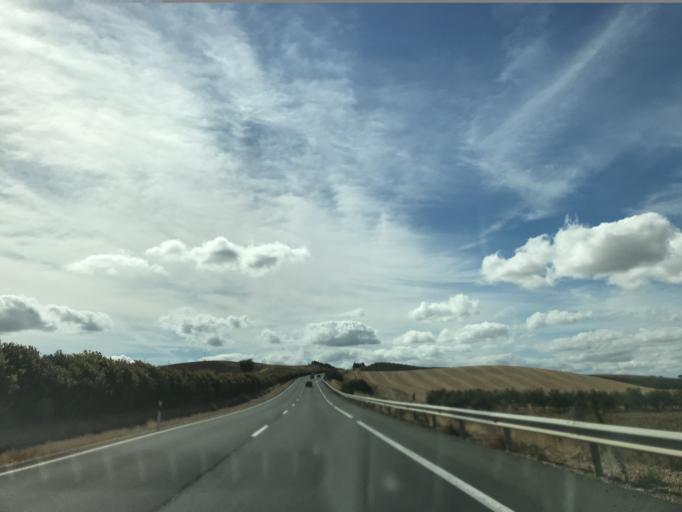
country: ES
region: Andalusia
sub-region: Province of Cordoba
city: La Victoria
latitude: 37.7325
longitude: -4.8535
